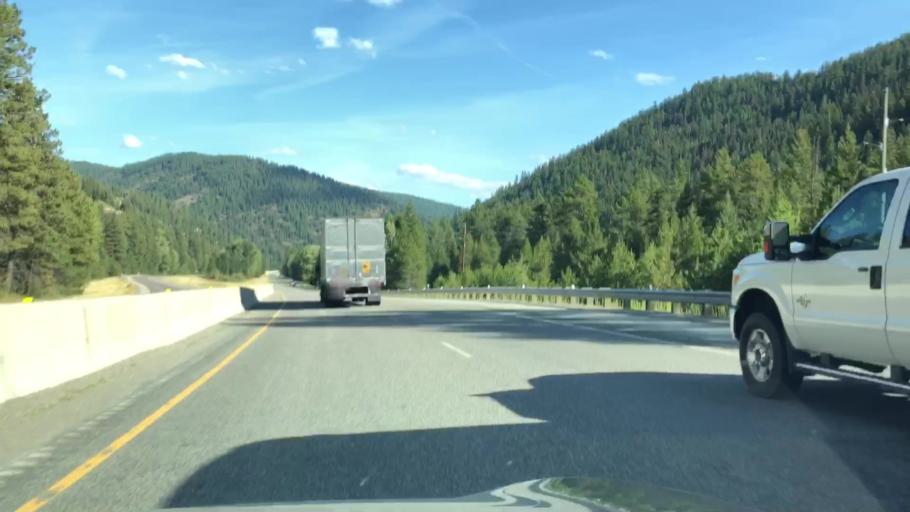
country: US
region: Montana
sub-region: Sanders County
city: Thompson Falls
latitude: 47.3599
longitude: -115.3171
